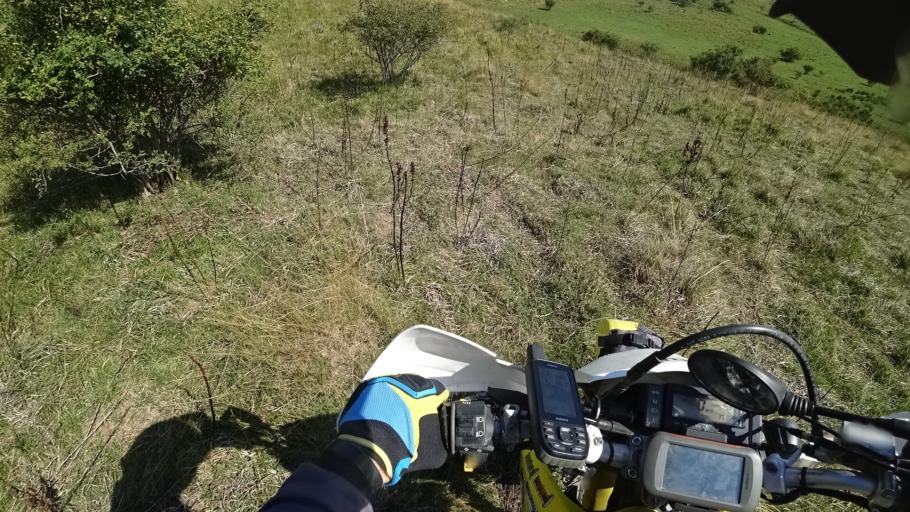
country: HR
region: Zadarska
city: Gracac
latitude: 44.4011
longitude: 16.0095
